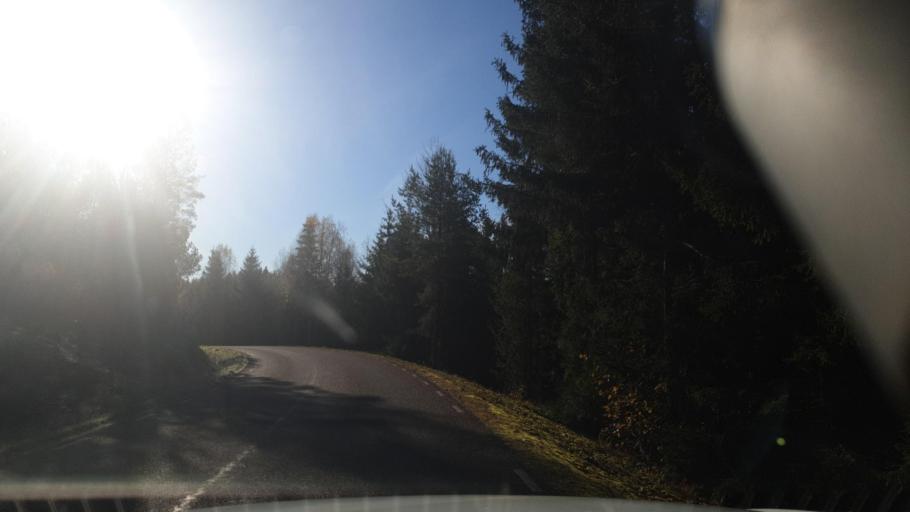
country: SE
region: Vaermland
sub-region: Karlstads Kommun
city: Valberg
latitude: 59.4571
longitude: 13.0837
